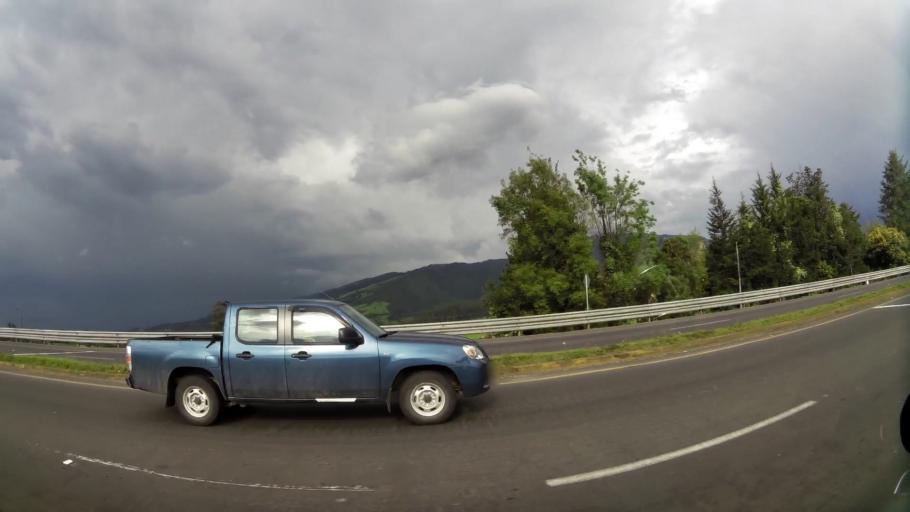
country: EC
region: Pichincha
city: Machachi
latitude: -0.4133
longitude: -78.5484
